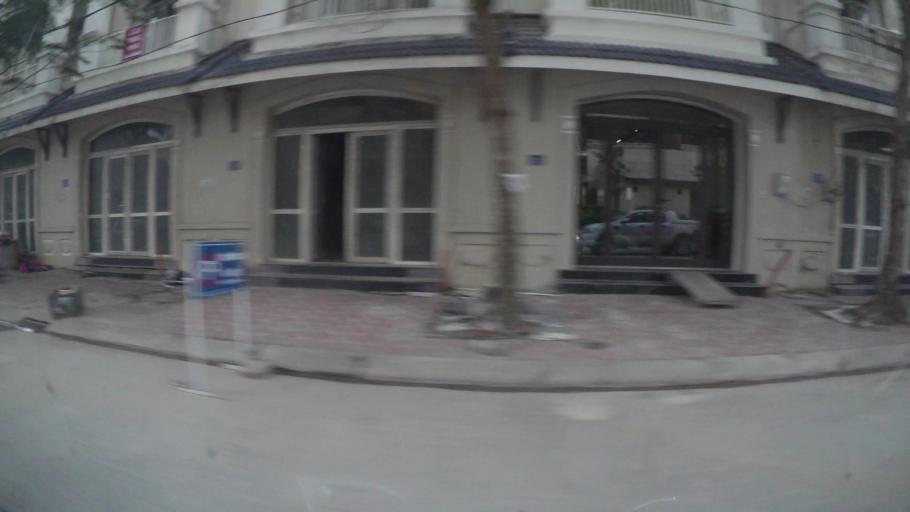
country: VN
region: Ha Noi
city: Cau Dien
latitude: 21.0029
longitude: 105.7315
